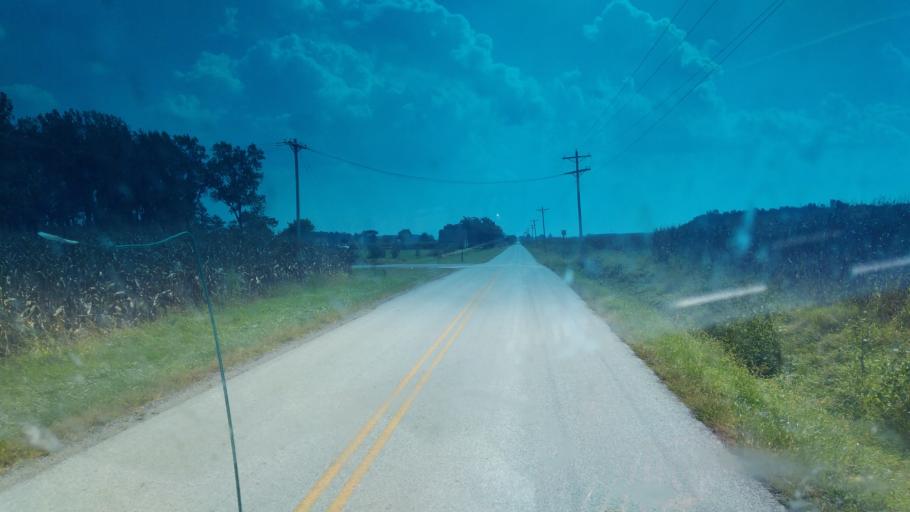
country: US
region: Ohio
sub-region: Hardin County
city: Kenton
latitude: 40.6591
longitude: -83.7264
